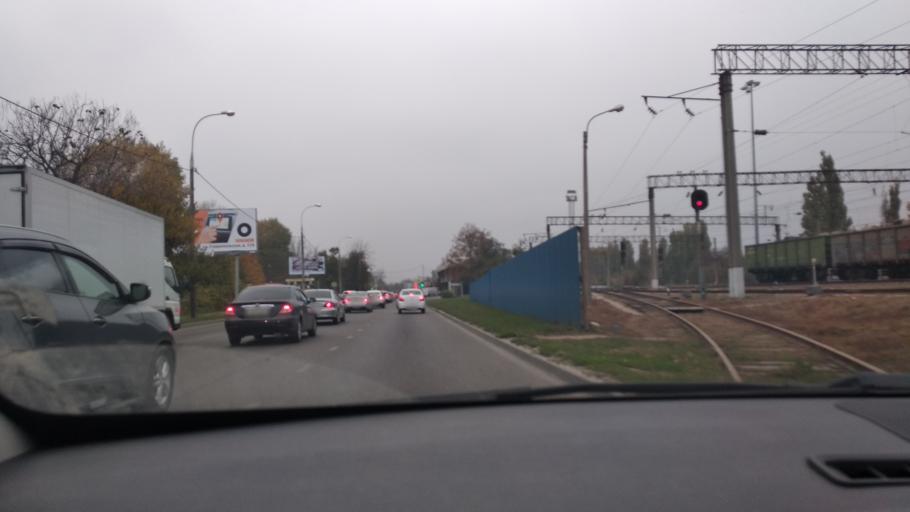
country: RU
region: Krasnodarskiy
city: Krasnodar
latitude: 45.0362
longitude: 39.0393
